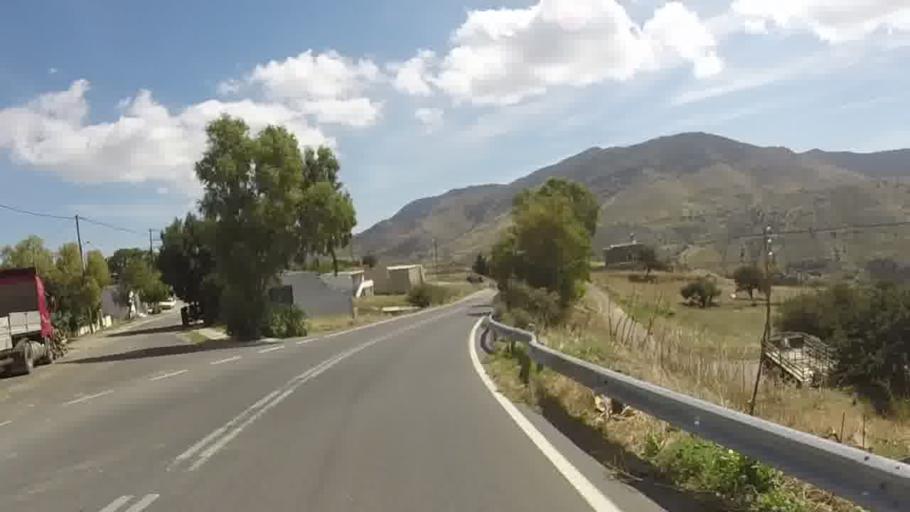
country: GR
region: Crete
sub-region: Nomos Rethymnis
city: Agia Galini
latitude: 35.1501
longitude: 24.6272
